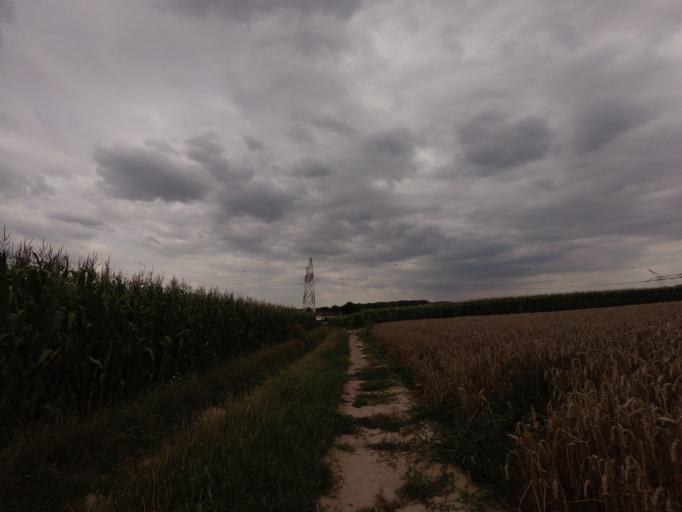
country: BE
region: Flanders
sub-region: Provincie Vlaams-Brabant
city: Grimbergen
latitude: 50.9233
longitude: 4.3853
